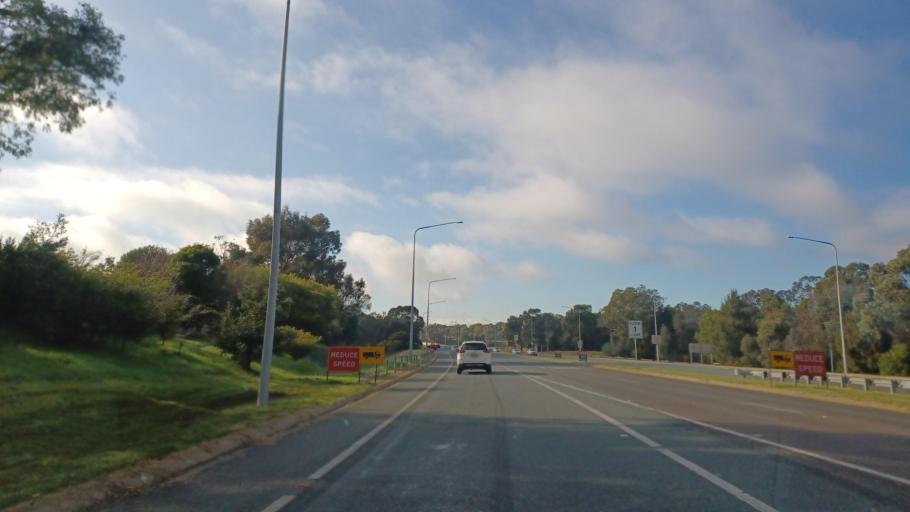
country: AU
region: Australian Capital Territory
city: Belconnen
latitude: -35.2215
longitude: 149.0628
